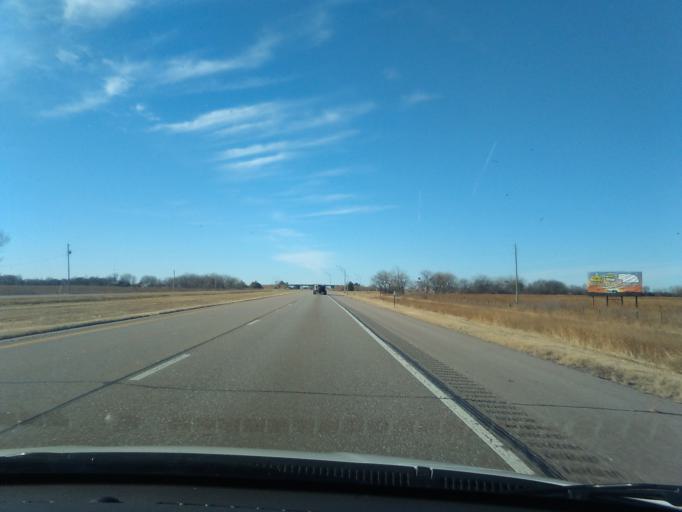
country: US
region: Nebraska
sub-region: Hall County
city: Wood River
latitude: 40.8015
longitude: -98.4833
